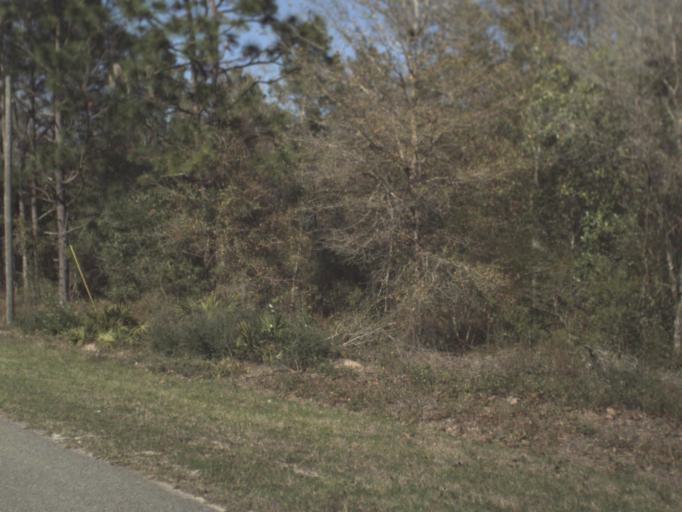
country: US
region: Florida
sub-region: Gulf County
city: Wewahitchka
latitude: 30.1840
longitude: -85.2057
